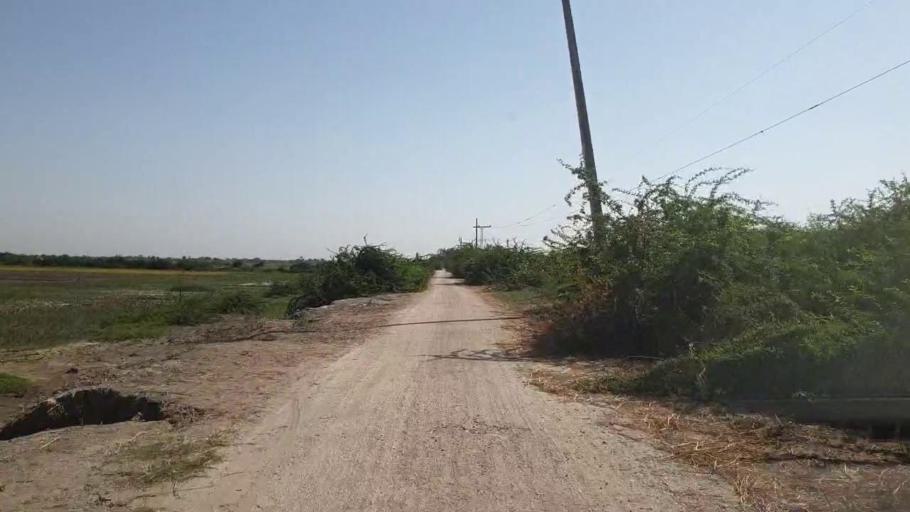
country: PK
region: Sindh
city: Tando Bago
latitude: 24.6438
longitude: 68.9876
